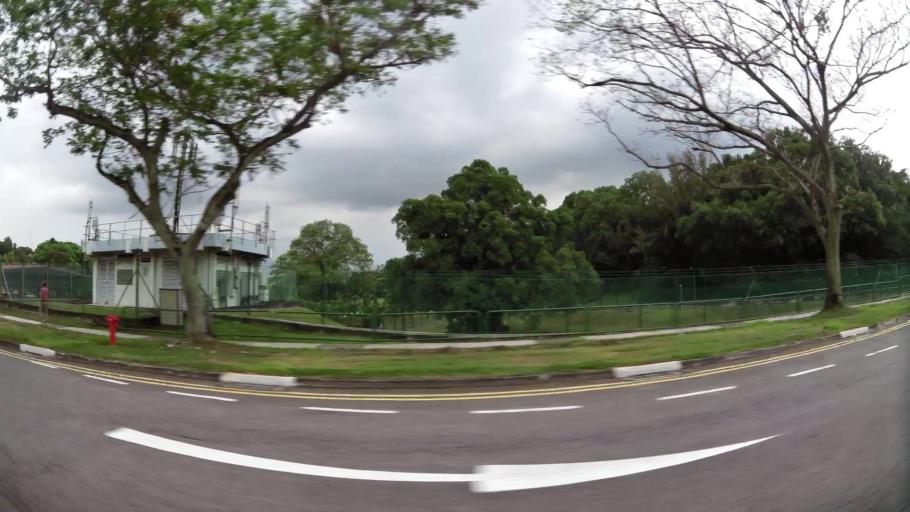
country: MY
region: Johor
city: Kampung Pasir Gudang Baru
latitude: 1.4580
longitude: 103.8292
